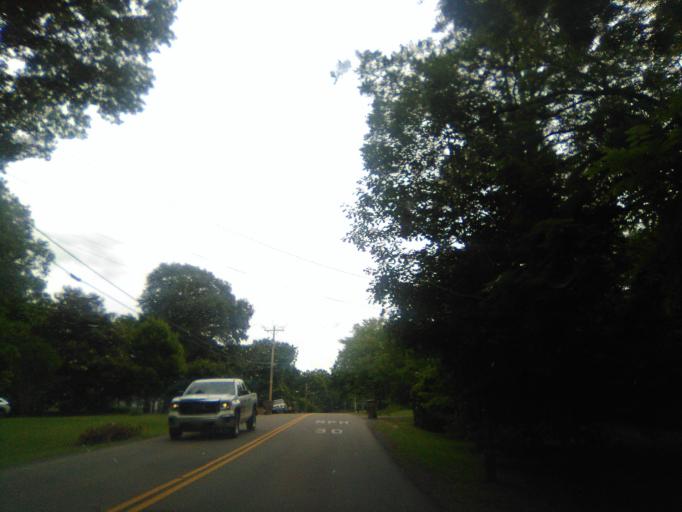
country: US
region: Tennessee
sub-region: Davidson County
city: Belle Meade
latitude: 36.1215
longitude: -86.8850
